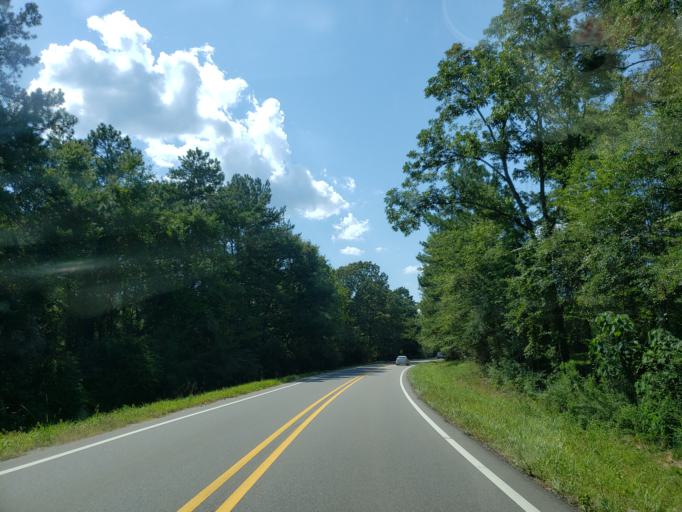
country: US
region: Mississippi
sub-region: Lamar County
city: Sumrall
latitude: 31.3797
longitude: -89.5231
